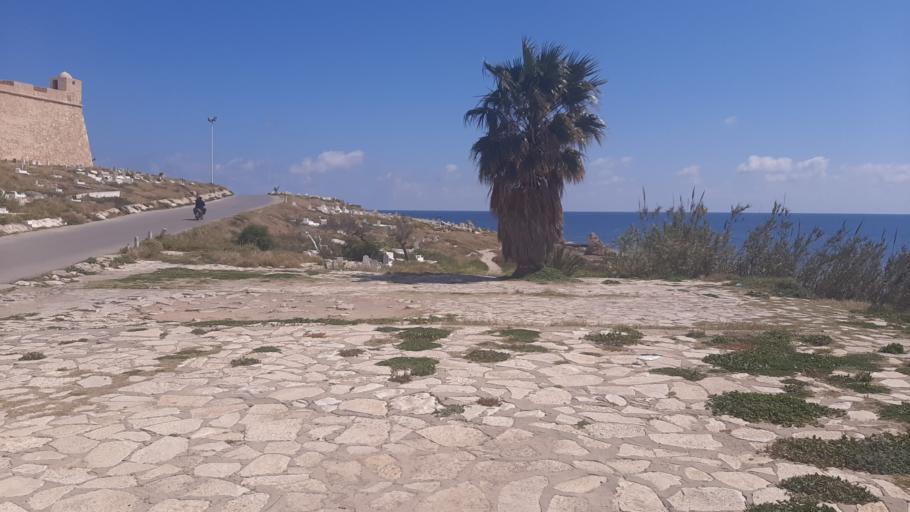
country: TN
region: Al Mahdiyah
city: Mahdia
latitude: 35.5044
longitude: 11.0760
